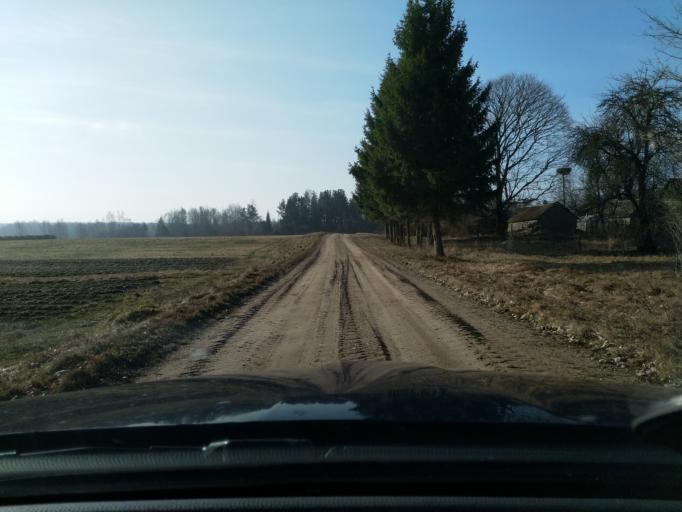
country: LV
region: Kuldigas Rajons
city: Kuldiga
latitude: 56.8758
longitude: 21.9640
